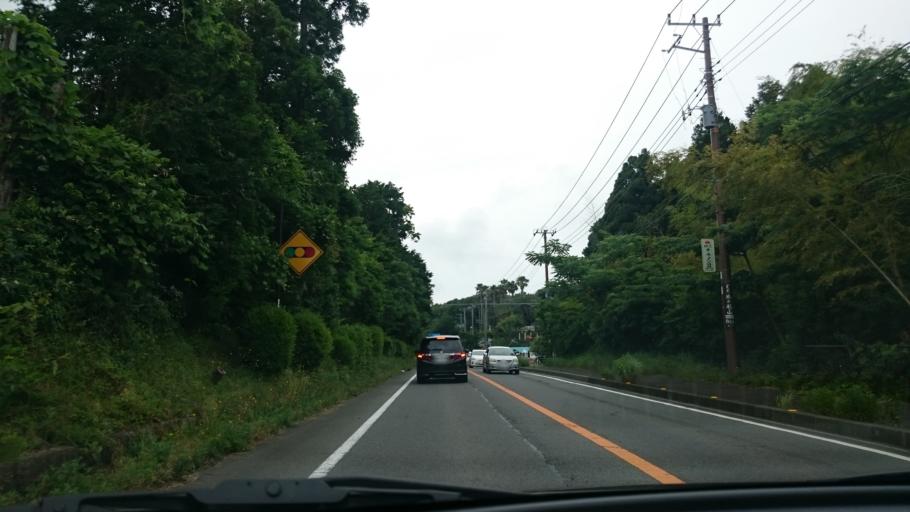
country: JP
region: Shizuoka
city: Ito
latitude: 34.9204
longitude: 139.1196
